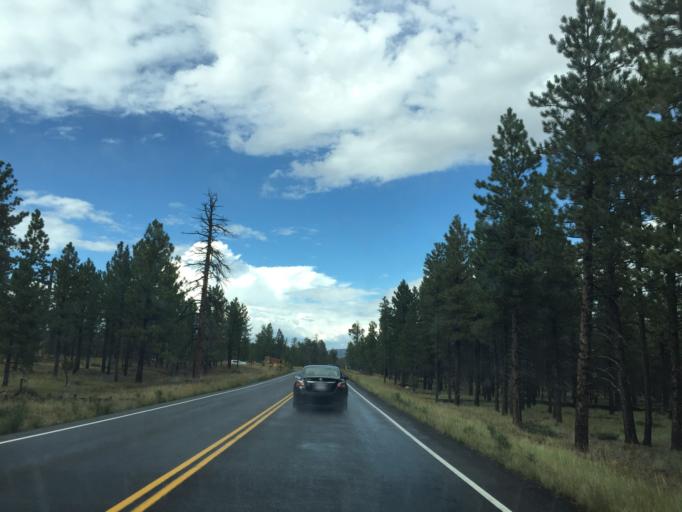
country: US
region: Utah
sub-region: Garfield County
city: Panguitch
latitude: 37.6537
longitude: -112.1632
